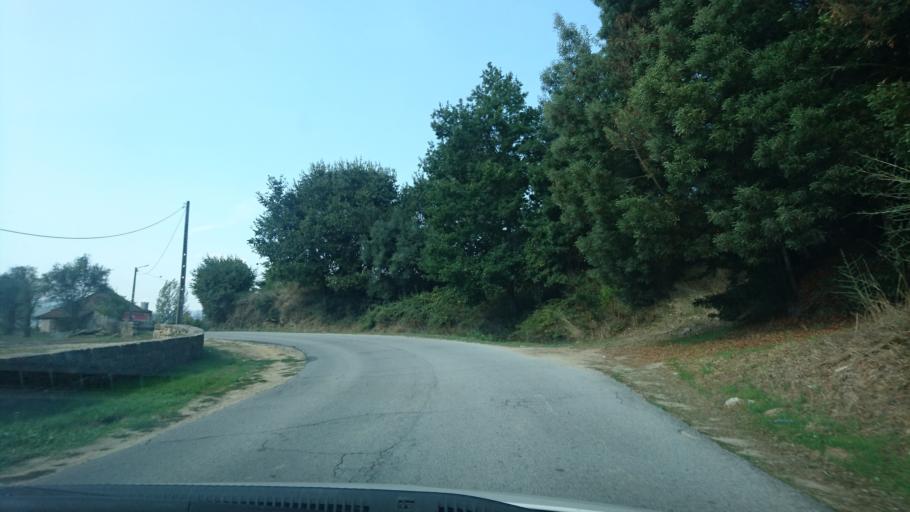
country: PT
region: Vila Real
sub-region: Mondim de Basto
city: Mondim de Basto
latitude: 41.4552
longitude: -7.9227
